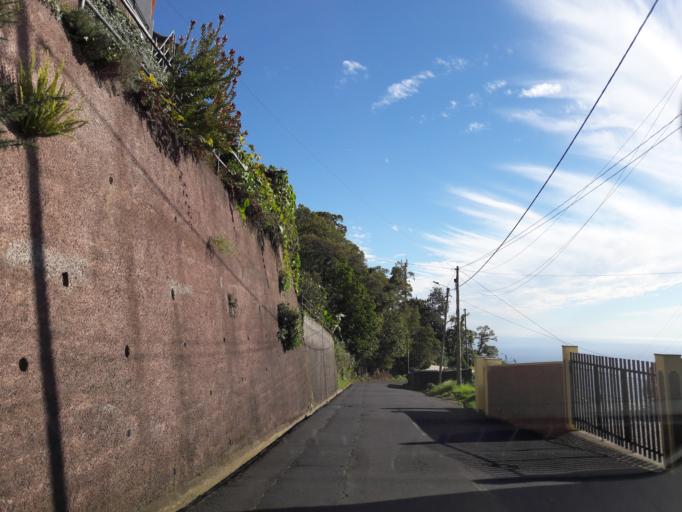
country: PT
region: Madeira
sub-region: Funchal
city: Nossa Senhora do Monte
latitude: 32.6787
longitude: -16.9119
